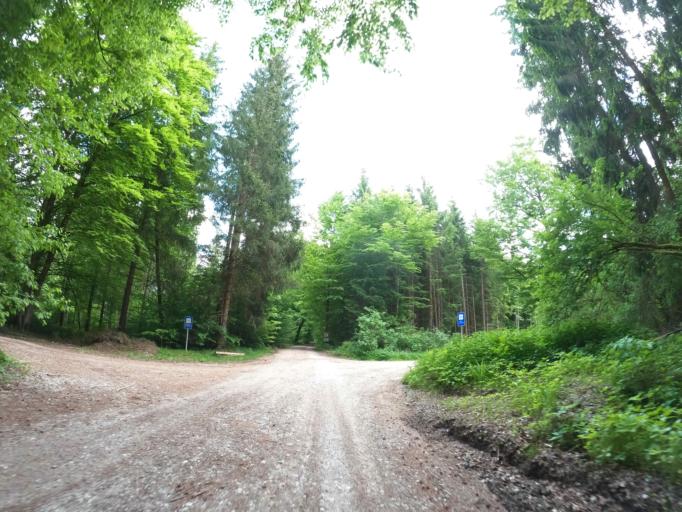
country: DE
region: Bavaria
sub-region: Upper Bavaria
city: Brunnthal
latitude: 47.9709
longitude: 11.7128
